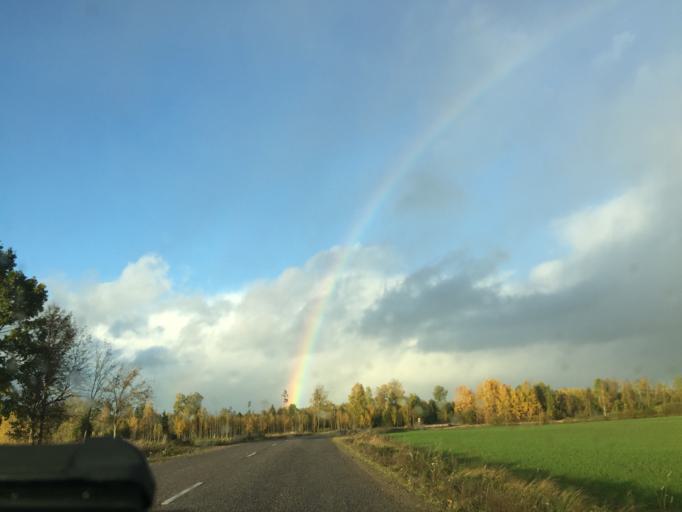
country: LV
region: Broceni
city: Broceni
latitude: 56.8821
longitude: 22.3838
